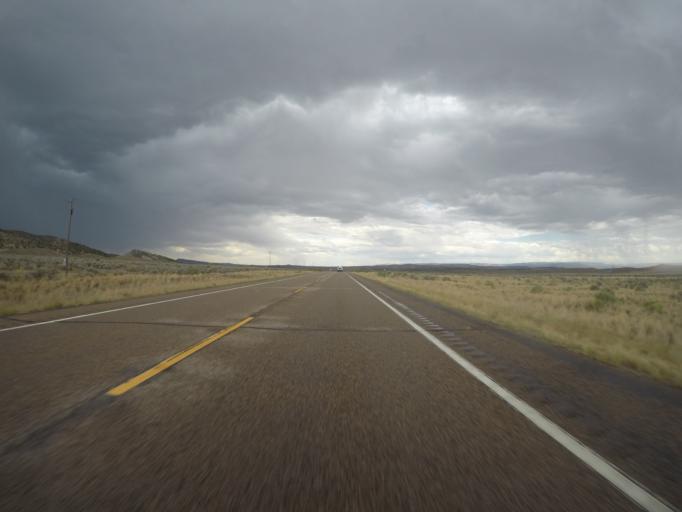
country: US
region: Colorado
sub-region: Rio Blanco County
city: Rangely
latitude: 40.2388
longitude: -108.9183
